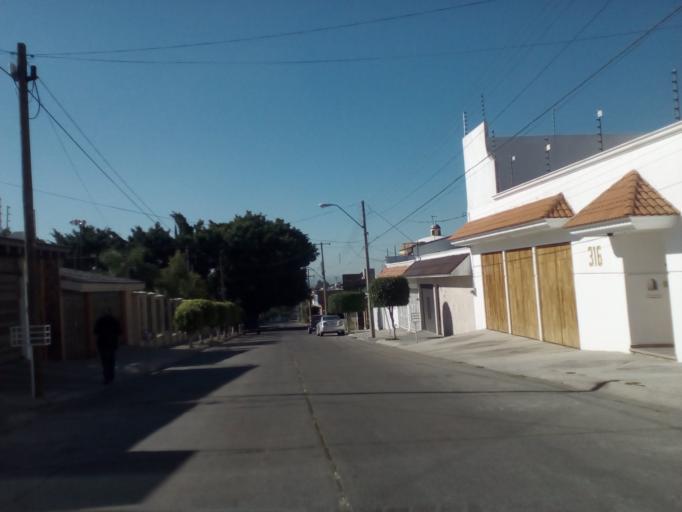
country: MX
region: Guanajuato
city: Leon
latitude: 21.1192
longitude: -101.7013
